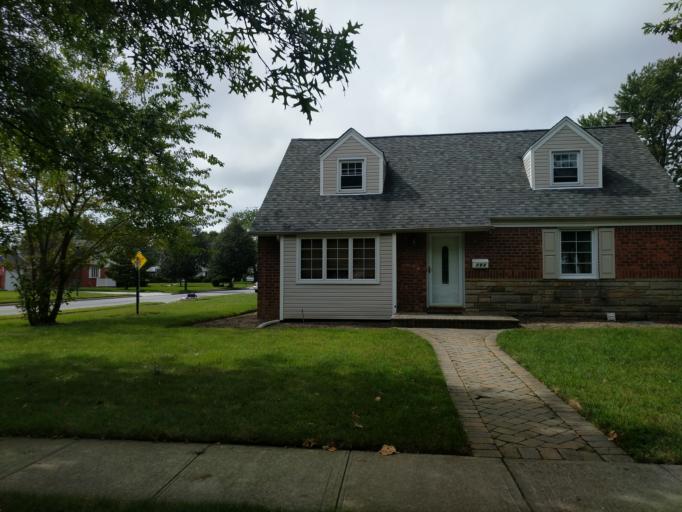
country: US
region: New York
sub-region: Nassau County
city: Malverne
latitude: 40.6860
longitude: -73.6681
